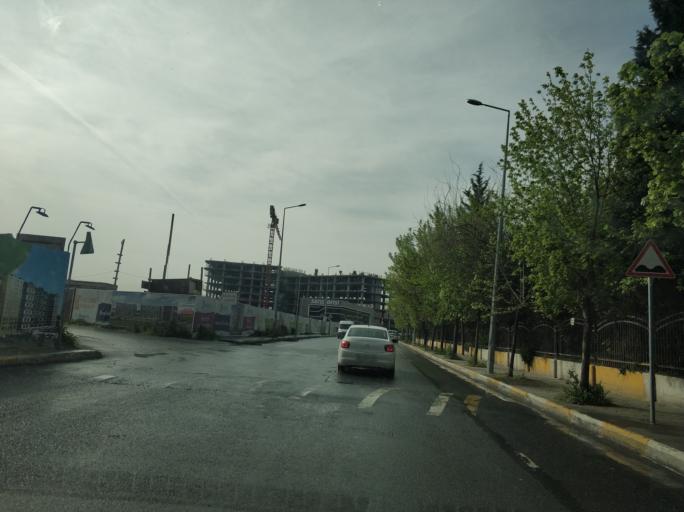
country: TR
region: Istanbul
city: Bahcelievler
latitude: 41.0022
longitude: 28.8094
